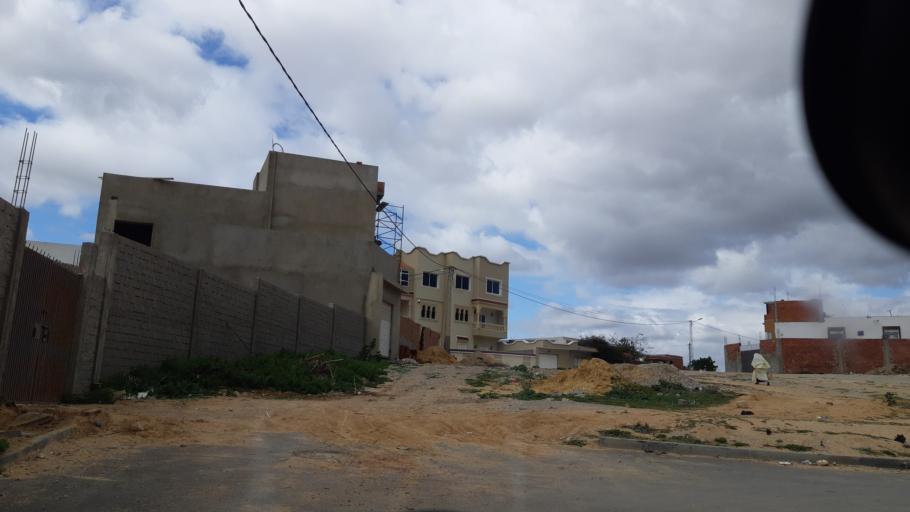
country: TN
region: Susah
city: Akouda
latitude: 35.8702
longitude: 10.5204
